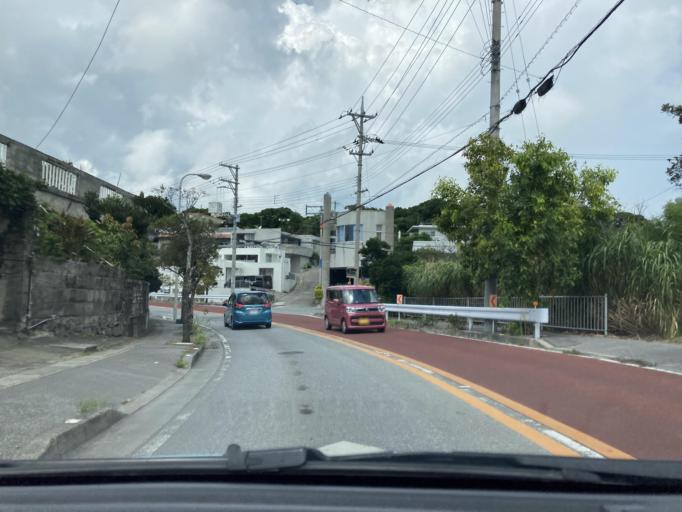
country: JP
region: Okinawa
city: Tomigusuku
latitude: 26.1700
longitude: 127.7545
